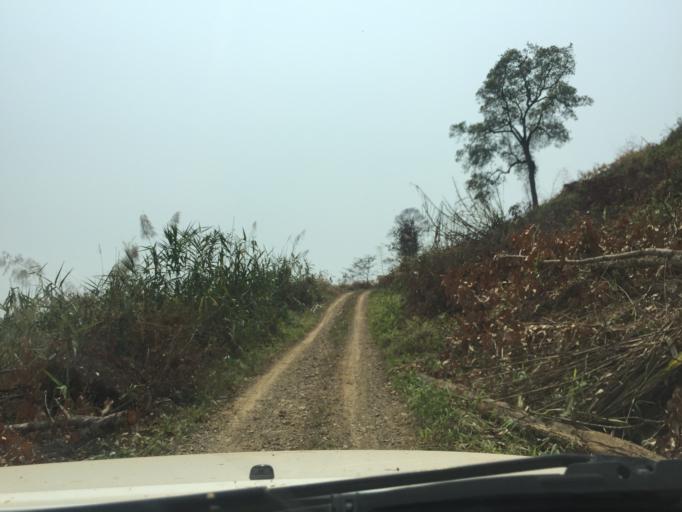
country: LA
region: Loungnamtha
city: Muang Nale
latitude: 20.6195
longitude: 101.6121
